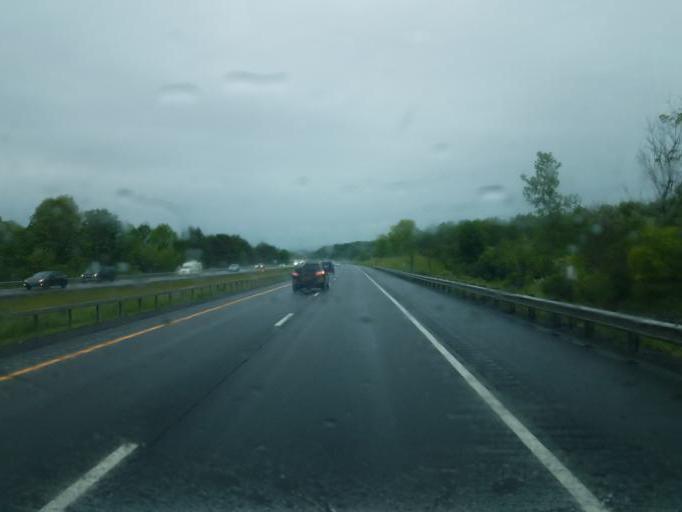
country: US
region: New York
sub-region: Herkimer County
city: Frankfort
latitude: 43.0516
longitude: -75.0625
